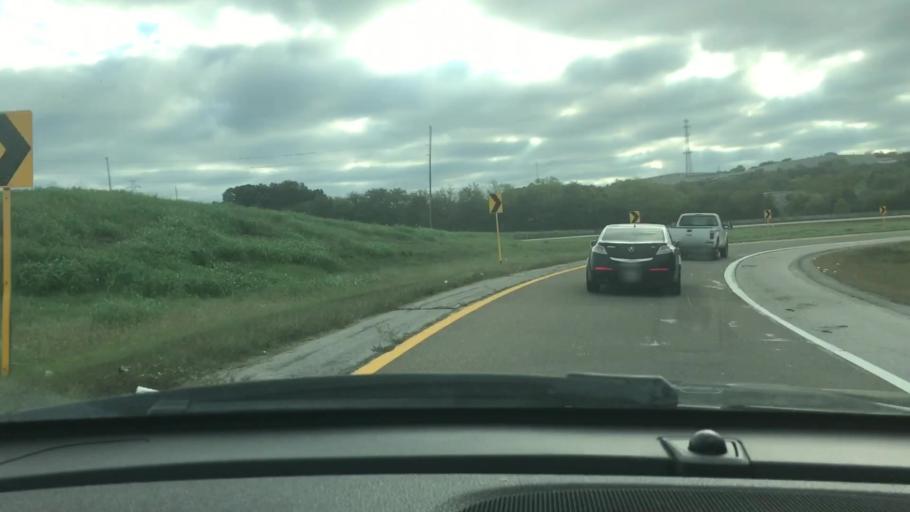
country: US
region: Tennessee
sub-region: Sumner County
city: Hendersonville
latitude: 36.3130
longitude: -86.6580
